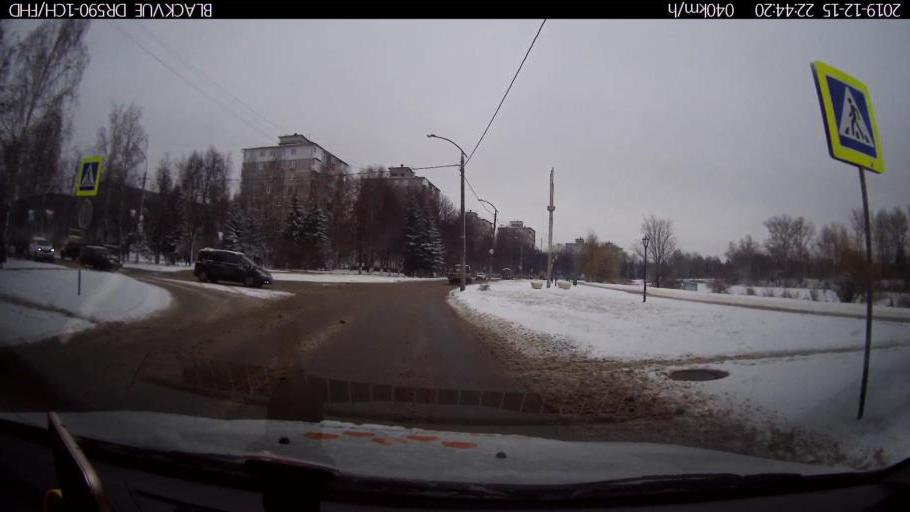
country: RU
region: Nizjnij Novgorod
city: Gorbatovka
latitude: 56.3458
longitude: 43.8516
